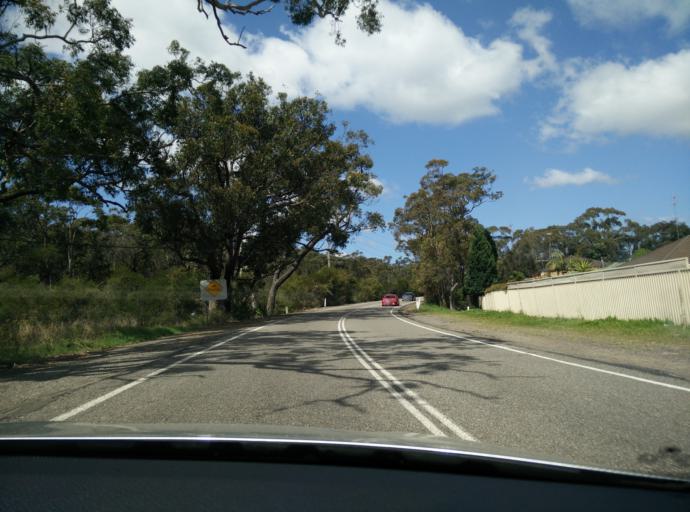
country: AU
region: New South Wales
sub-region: Gosford Shire
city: Point Clare
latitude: -33.4464
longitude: 151.2932
